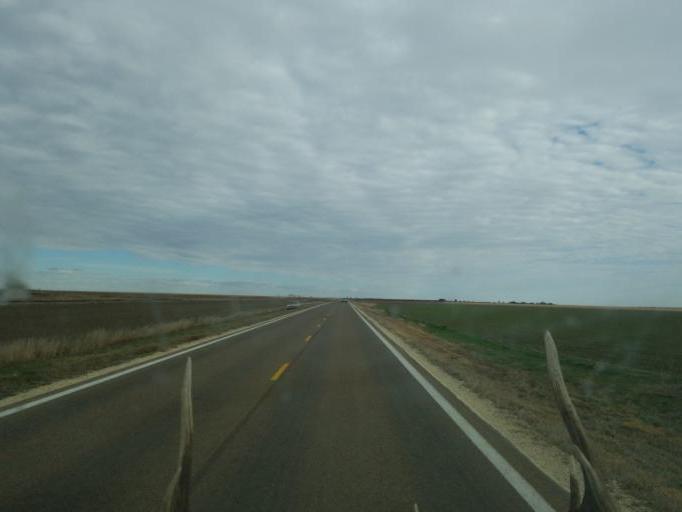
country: US
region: Kansas
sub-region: Logan County
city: Oakley
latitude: 39.0903
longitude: -101.1373
